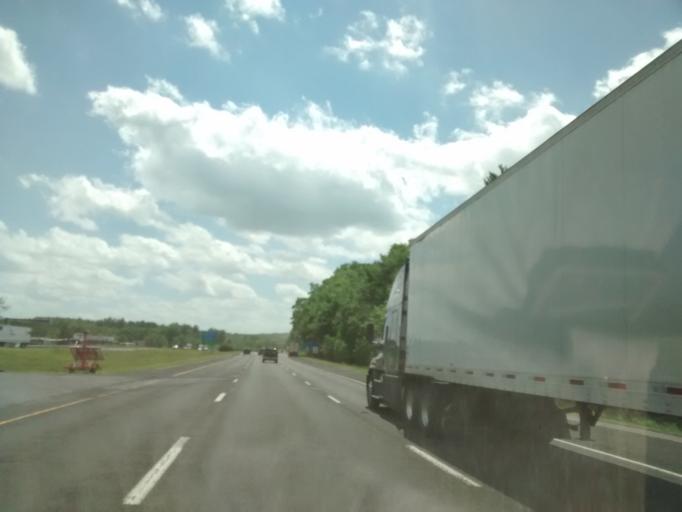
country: US
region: Massachusetts
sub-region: Hampden County
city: Holland
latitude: 42.0319
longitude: -72.1354
